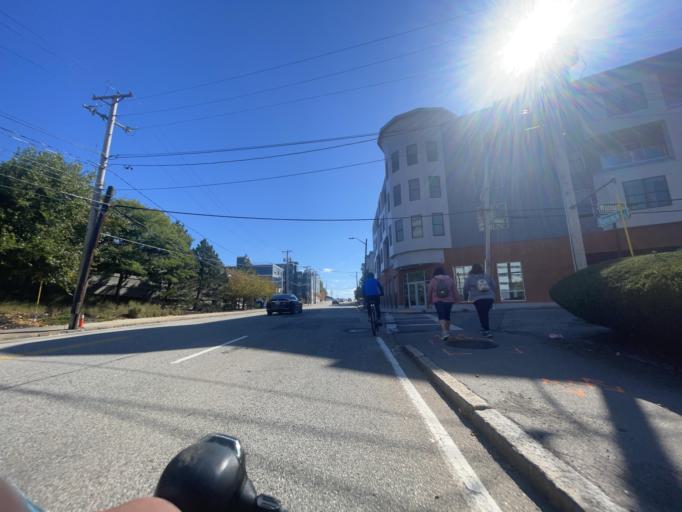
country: US
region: Massachusetts
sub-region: Norfolk County
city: Quincy
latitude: 42.2804
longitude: -71.0344
